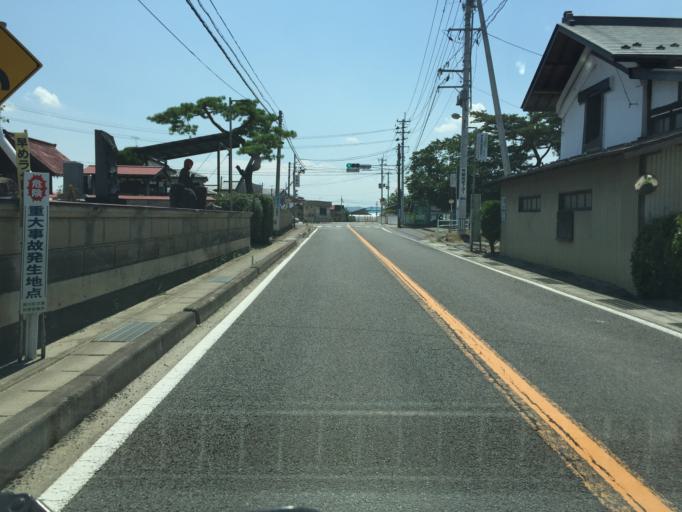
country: JP
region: Fukushima
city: Yanagawamachi-saiwaicho
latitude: 37.8423
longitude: 140.5842
